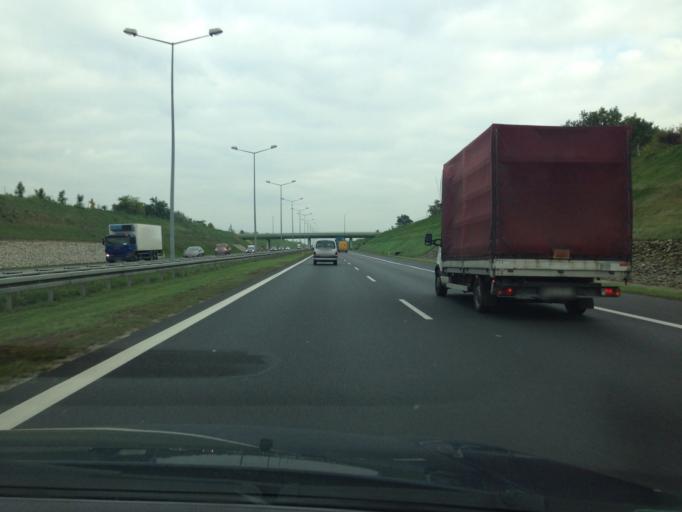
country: PL
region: Greater Poland Voivodeship
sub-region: Powiat poznanski
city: Czapury
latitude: 52.3510
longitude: 16.9374
